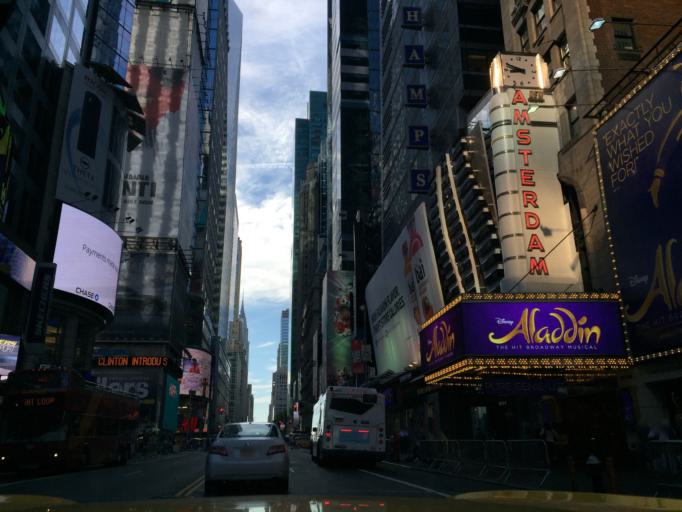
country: US
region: New York
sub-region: New York County
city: Manhattan
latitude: 40.7564
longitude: -73.9879
